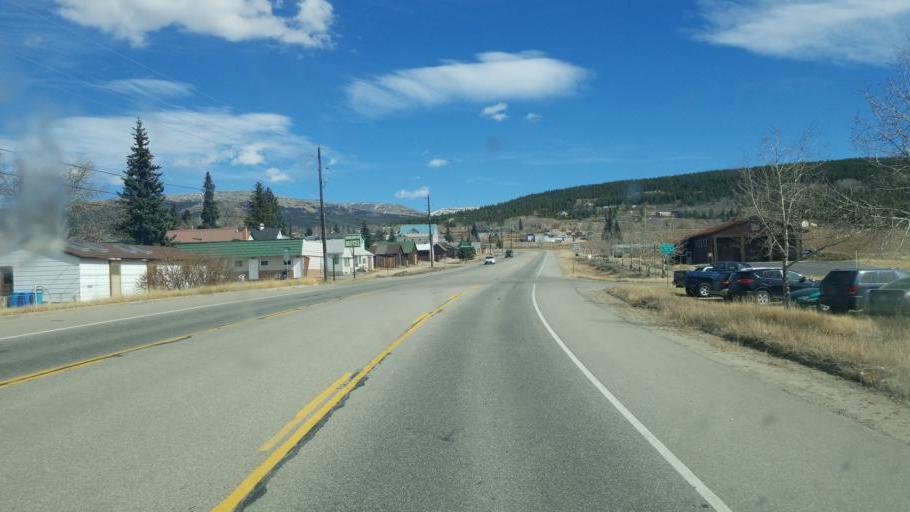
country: US
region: Colorado
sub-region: Lake County
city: Leadville
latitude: 39.2422
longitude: -106.2943
